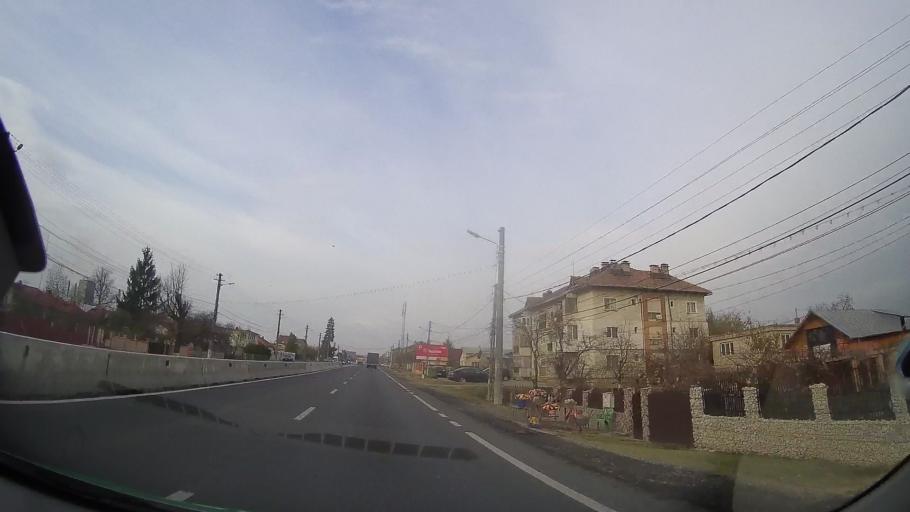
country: RO
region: Prahova
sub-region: Comuna Gorgota
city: Potigrafu
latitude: 44.7822
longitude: 26.0993
